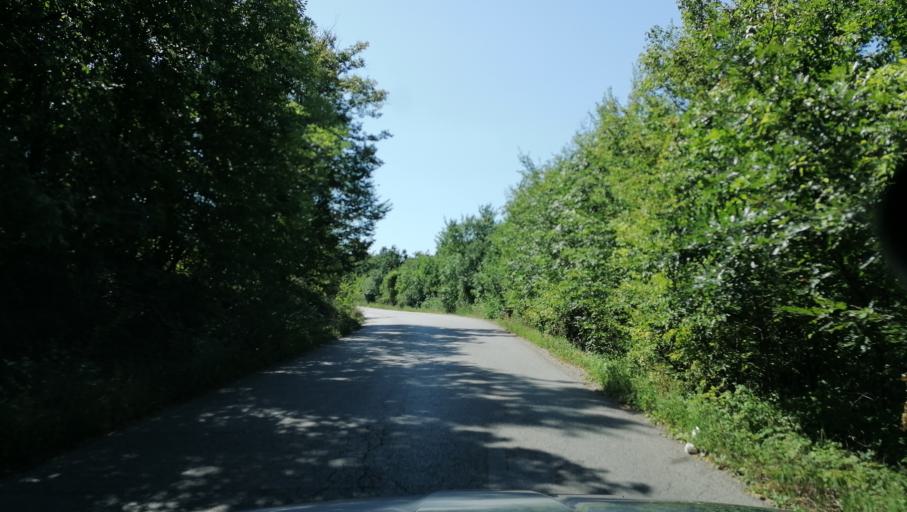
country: RS
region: Central Serbia
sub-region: Kolubarski Okrug
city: Valjevo
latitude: 44.2438
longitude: 19.8630
